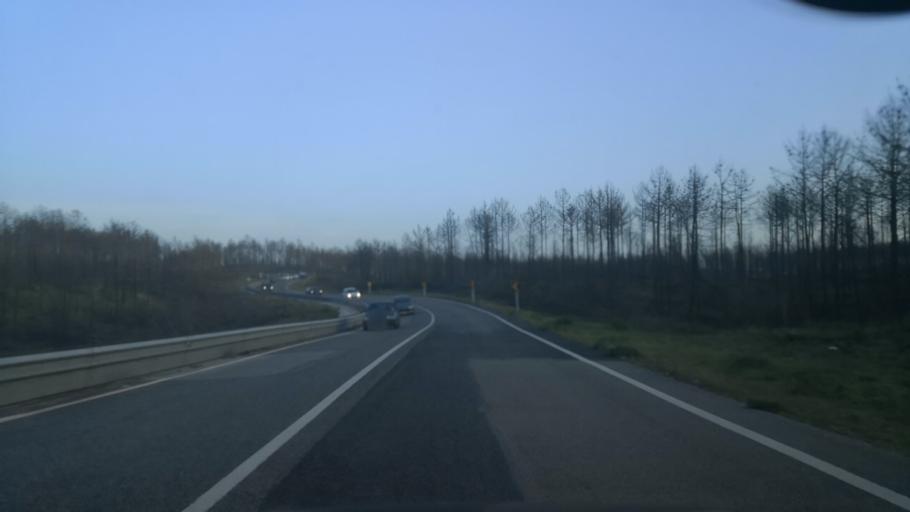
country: PT
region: Leiria
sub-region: Marinha Grande
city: Marinha Grande
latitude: 39.7476
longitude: -8.9999
